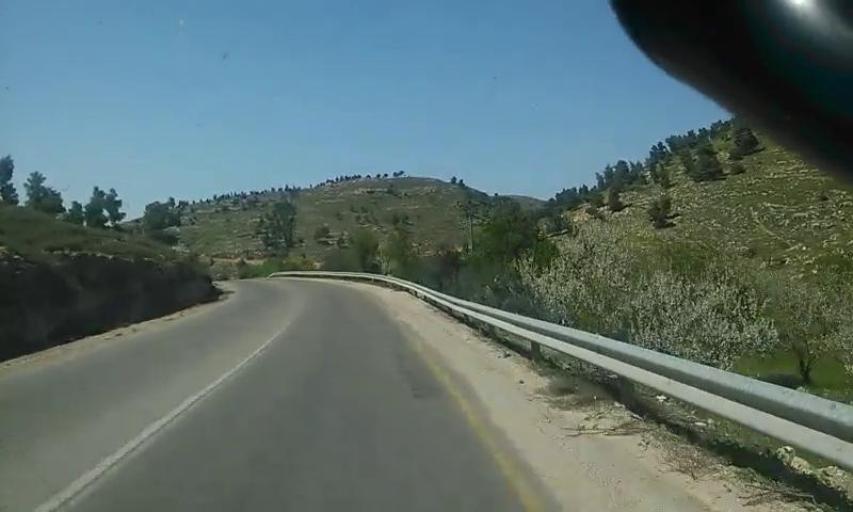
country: PS
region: West Bank
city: Ar Rihiyah
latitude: 31.4916
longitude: 35.0679
